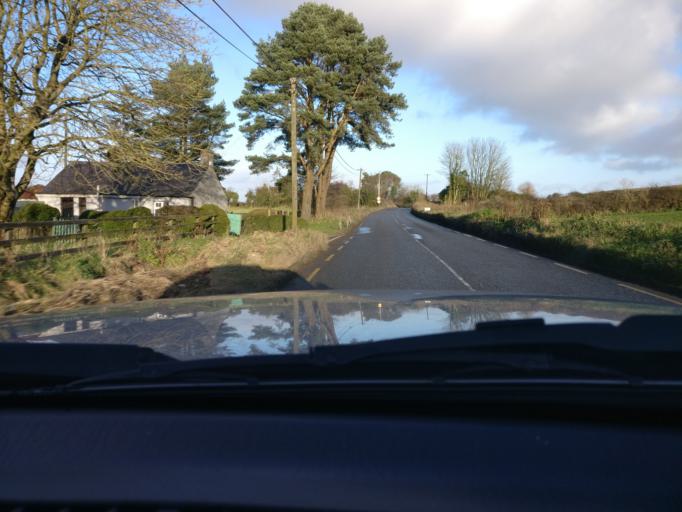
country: IE
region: Ulster
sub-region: An Cabhan
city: Mullagh
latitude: 53.7232
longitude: -6.9963
